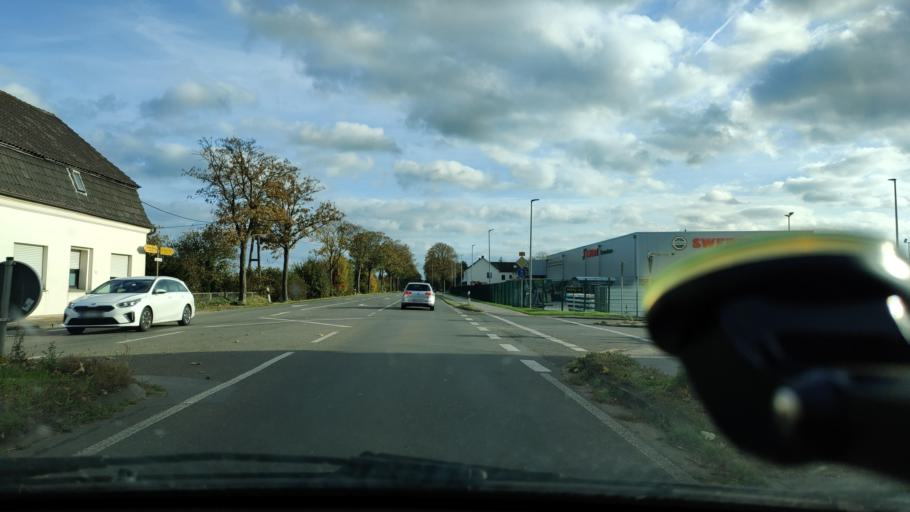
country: DE
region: North Rhine-Westphalia
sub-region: Regierungsbezirk Dusseldorf
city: Alpen
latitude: 51.5997
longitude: 6.5282
